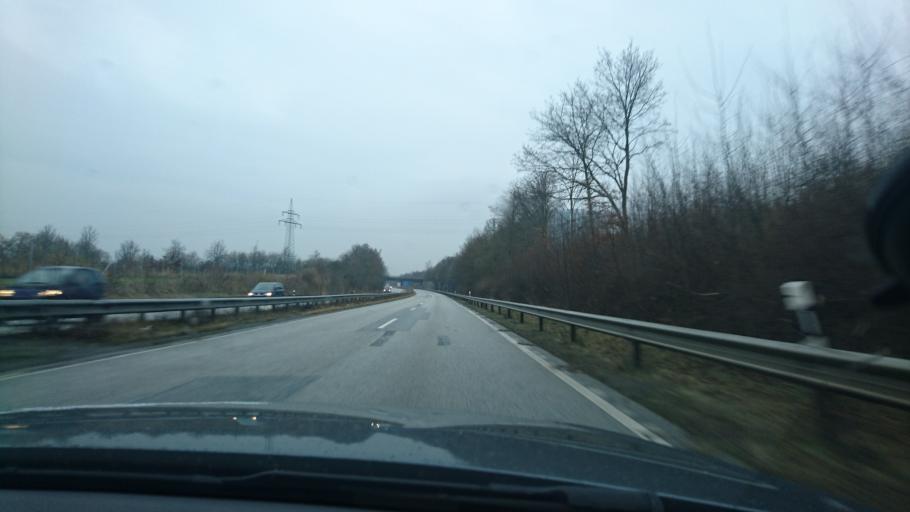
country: DE
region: Schleswig-Holstein
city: Oldenburg in Holstein
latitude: 54.2744
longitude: 10.8837
